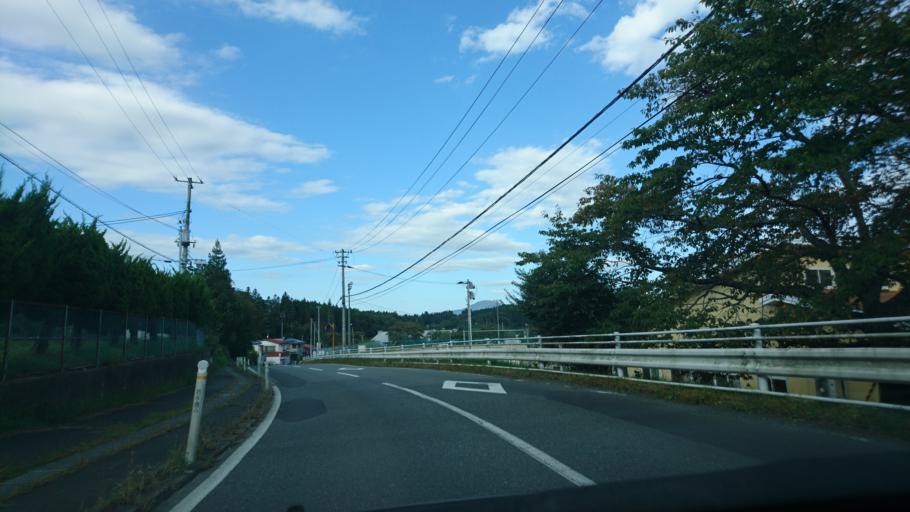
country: JP
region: Iwate
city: Ichinoseki
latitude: 38.8658
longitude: 141.3494
